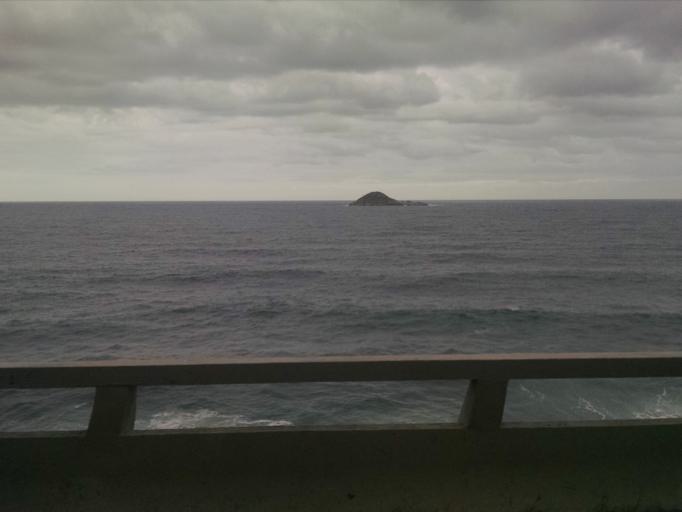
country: BR
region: Rio de Janeiro
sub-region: Rio De Janeiro
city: Rio de Janeiro
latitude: -23.0059
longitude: -43.2810
